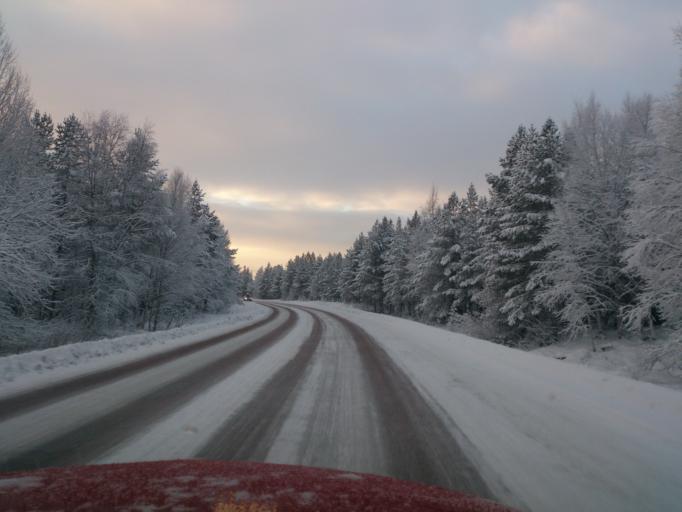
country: SE
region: Jaemtland
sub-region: Harjedalens Kommun
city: Sveg
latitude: 62.4712
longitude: 13.8759
